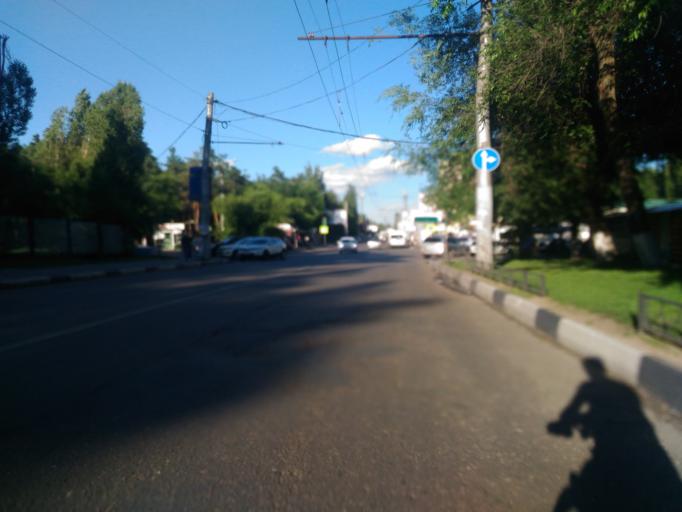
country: RU
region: Voronezj
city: Voronezh
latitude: 51.6516
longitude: 39.1275
